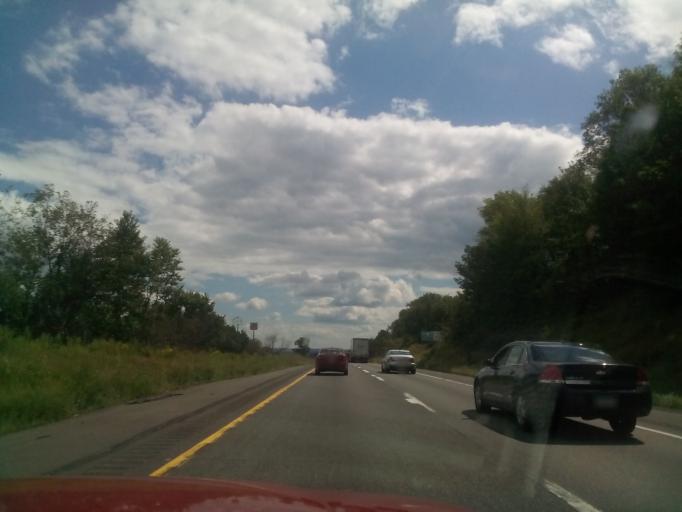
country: US
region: Pennsylvania
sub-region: Monroe County
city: Tannersville
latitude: 41.0443
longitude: -75.3142
